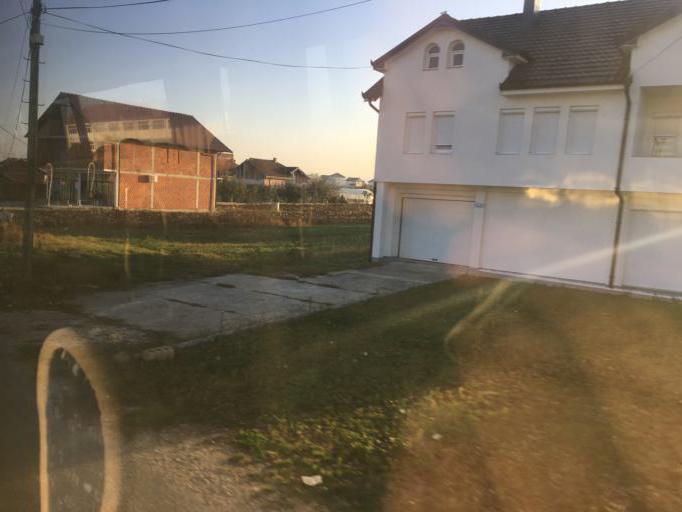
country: XK
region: Pristina
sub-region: Komuna e Drenasit
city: Glogovac
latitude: 42.5982
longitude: 20.8930
